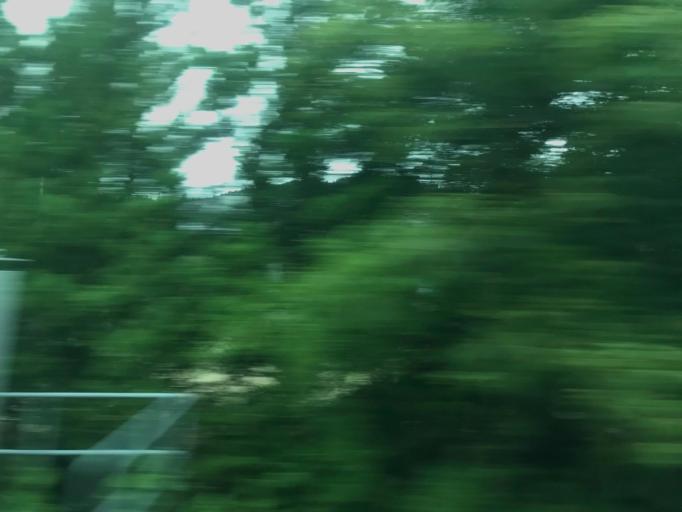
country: JP
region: Fukushima
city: Ishikawa
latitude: 37.1298
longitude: 140.2470
